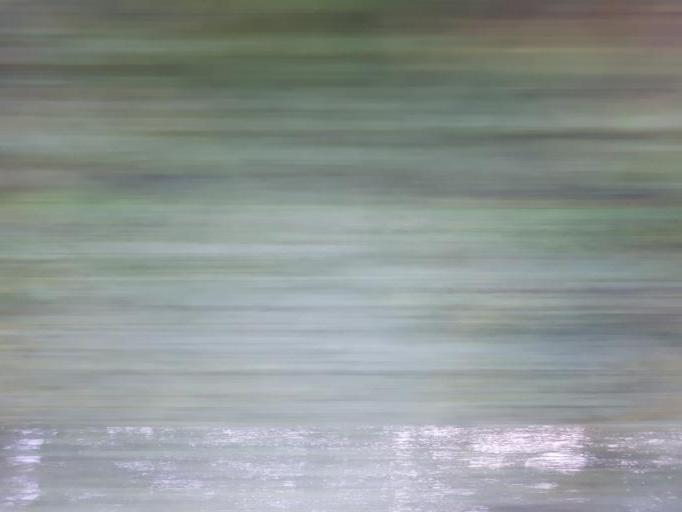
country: NO
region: Sor-Trondelag
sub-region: Melhus
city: Lundamo
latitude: 63.1517
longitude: 10.2830
